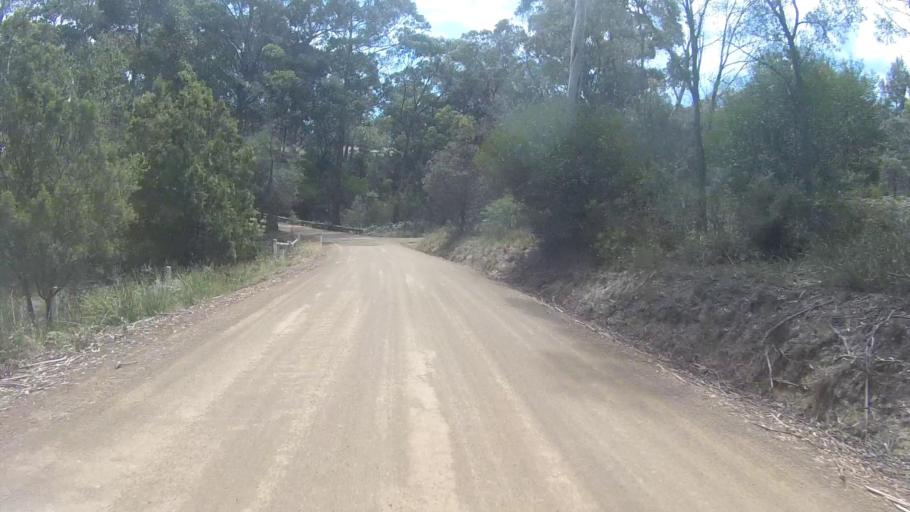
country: AU
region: Tasmania
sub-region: Kingborough
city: Blackmans Bay
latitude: -43.0467
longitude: 147.3075
